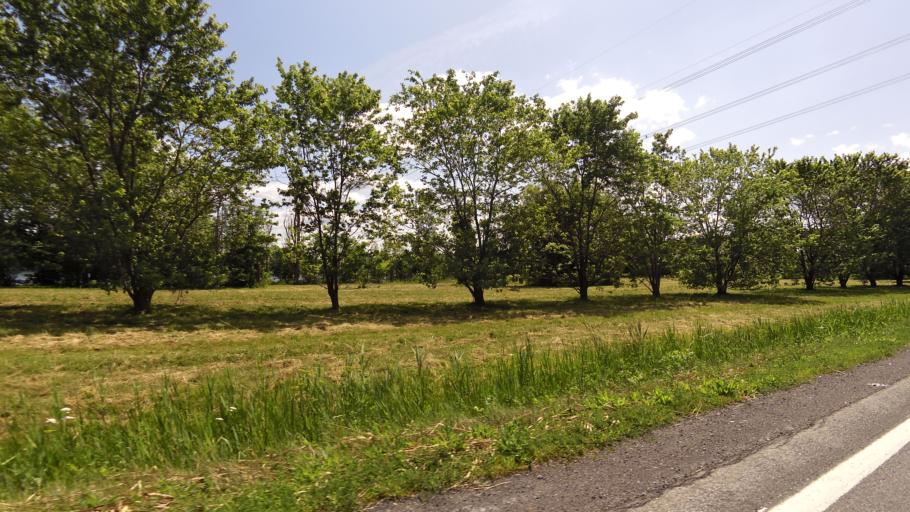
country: CA
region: Quebec
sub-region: Monteregie
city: Richelieu
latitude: 45.4165
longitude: -73.2456
